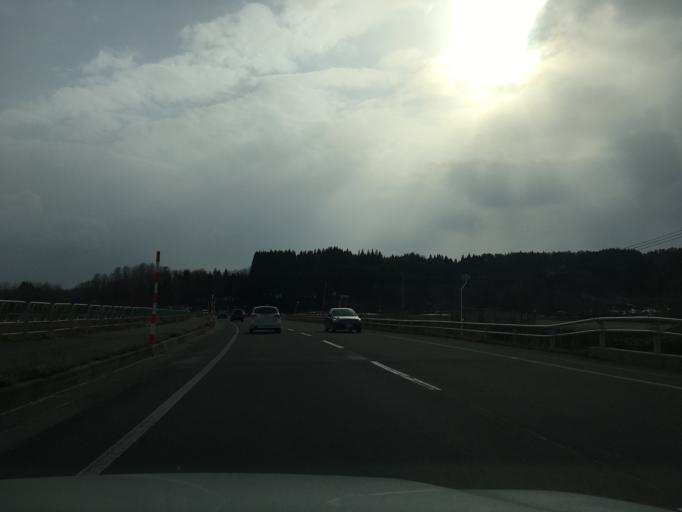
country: JP
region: Aomori
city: Namioka
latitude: 40.7663
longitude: 140.5894
